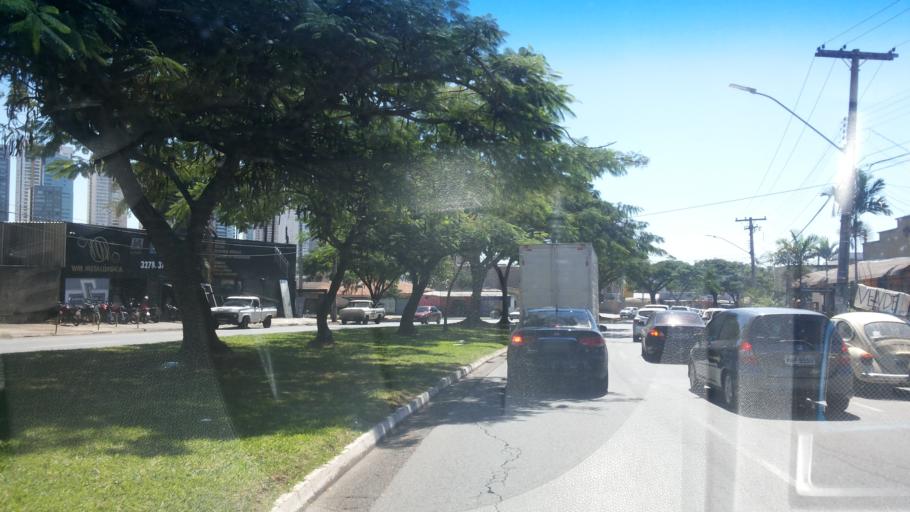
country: BR
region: Goias
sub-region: Goiania
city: Goiania
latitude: -16.7081
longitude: -49.2514
